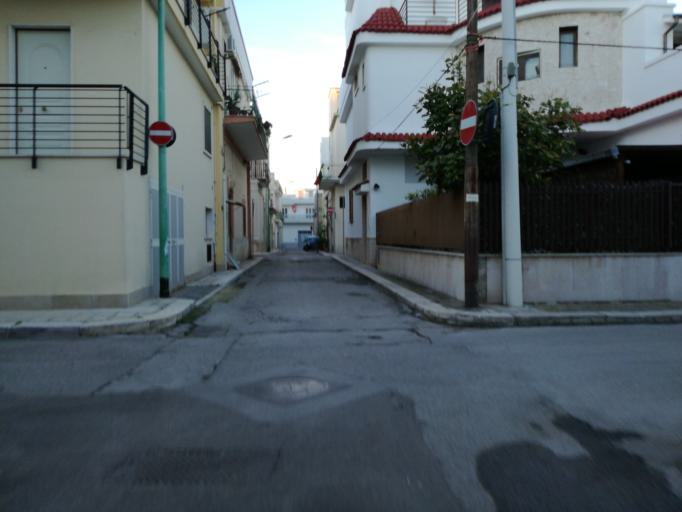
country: IT
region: Apulia
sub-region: Provincia di Bari
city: Adelfia
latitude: 41.0017
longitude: 16.8778
